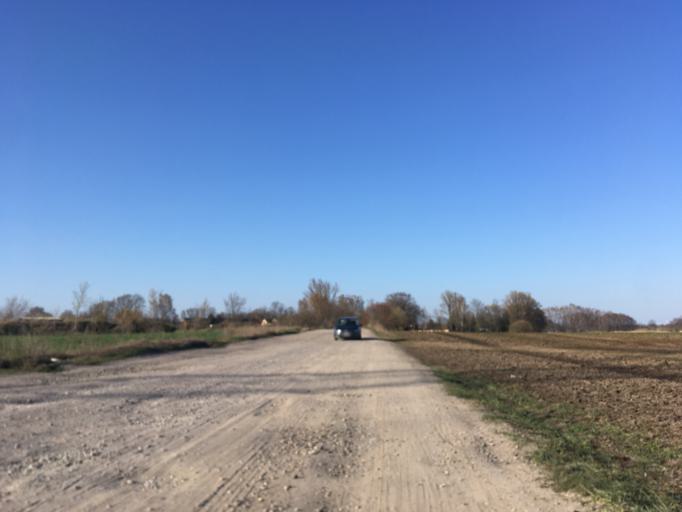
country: DE
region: Brandenburg
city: Ahrensfelde
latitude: 52.6211
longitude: 13.5743
